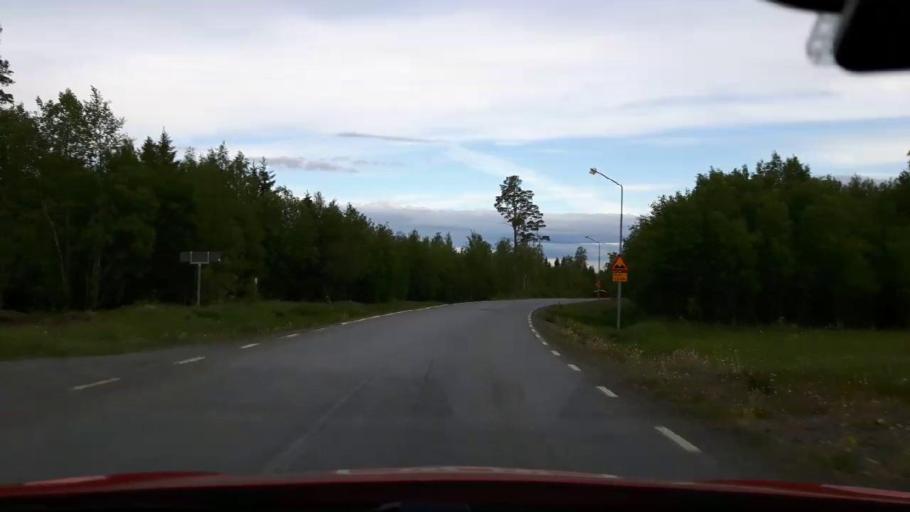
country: SE
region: Jaemtland
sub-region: Bergs Kommun
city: Hoverberg
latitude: 63.0099
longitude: 14.4933
